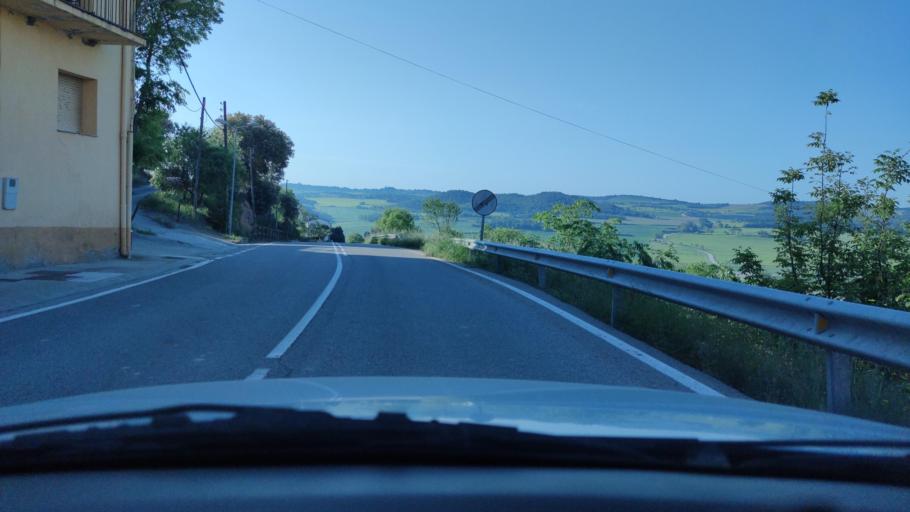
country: ES
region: Catalonia
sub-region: Provincia de Lleida
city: Artesa de Segre
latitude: 41.8767
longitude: 1.0148
